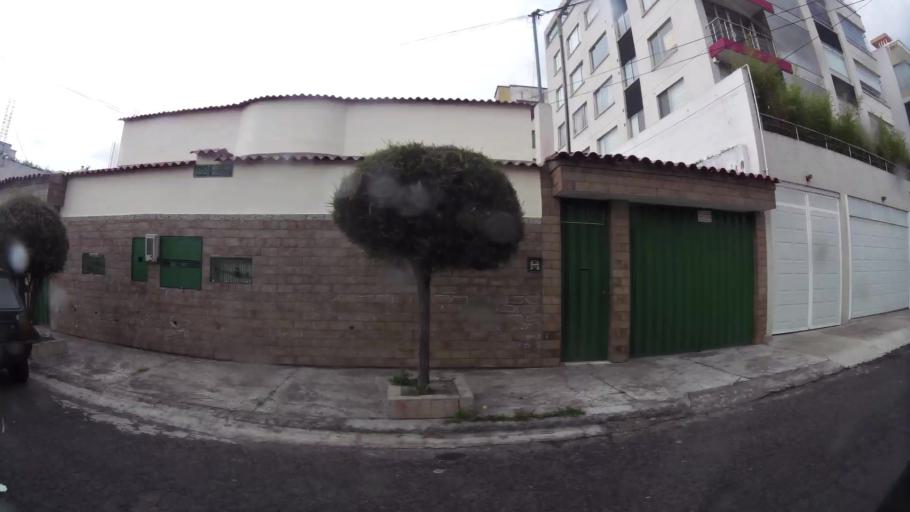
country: EC
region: Pichincha
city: Quito
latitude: -0.0988
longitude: -78.4810
